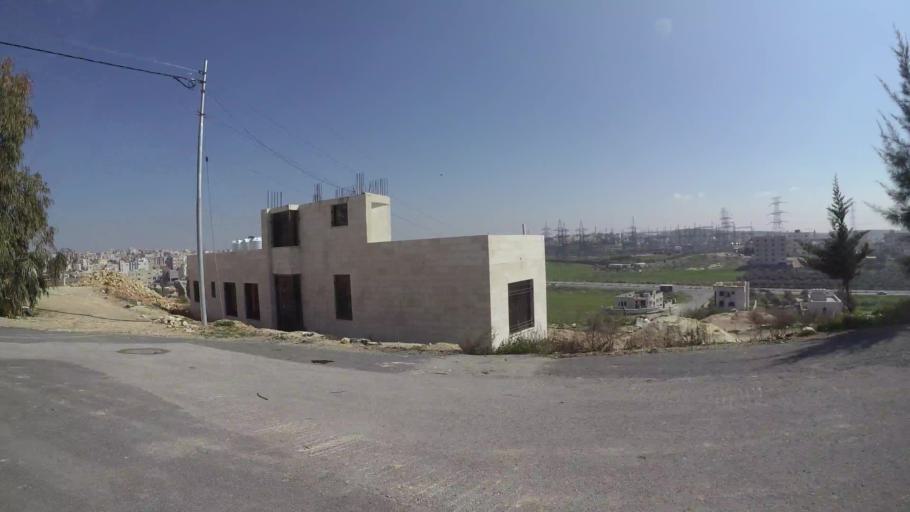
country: JO
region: Amman
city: Al Bunayyat ash Shamaliyah
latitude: 31.8930
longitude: 35.9008
